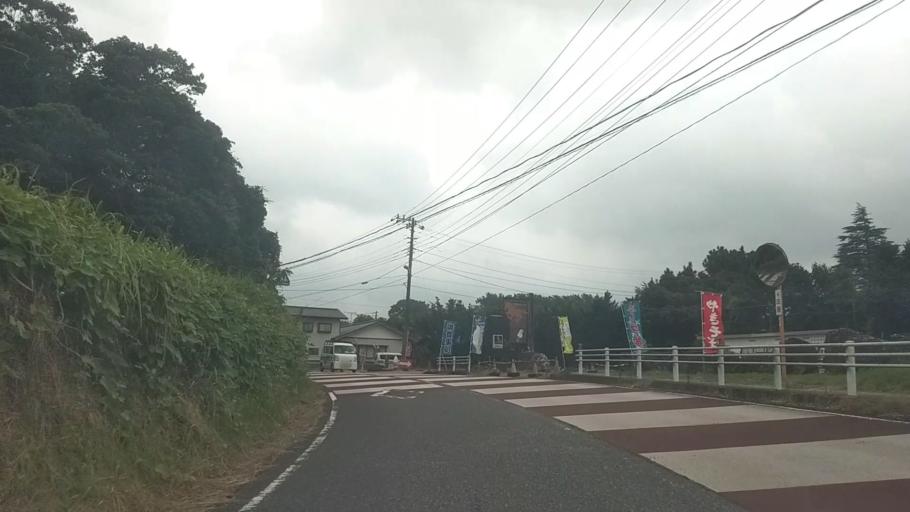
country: JP
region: Chiba
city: Kimitsu
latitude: 35.2362
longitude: 140.0011
